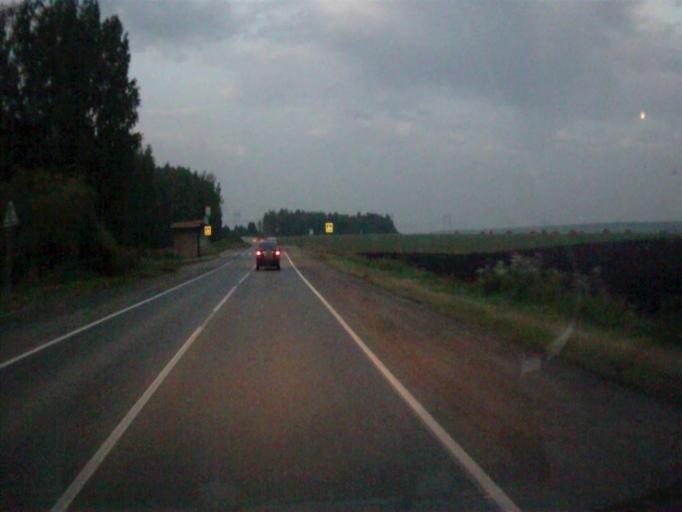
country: RU
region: Chelyabinsk
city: Argayash
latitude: 55.2096
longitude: 60.8677
